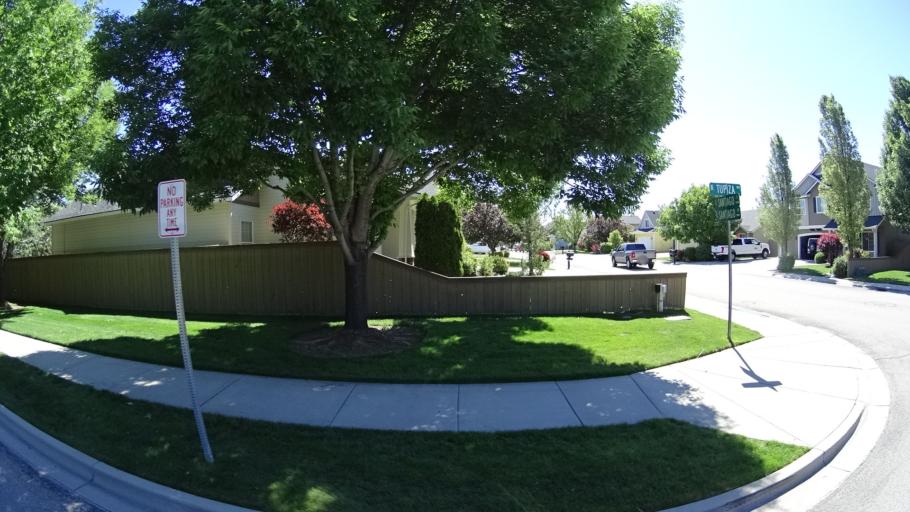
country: US
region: Idaho
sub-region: Ada County
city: Meridian
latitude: 43.6345
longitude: -116.3906
